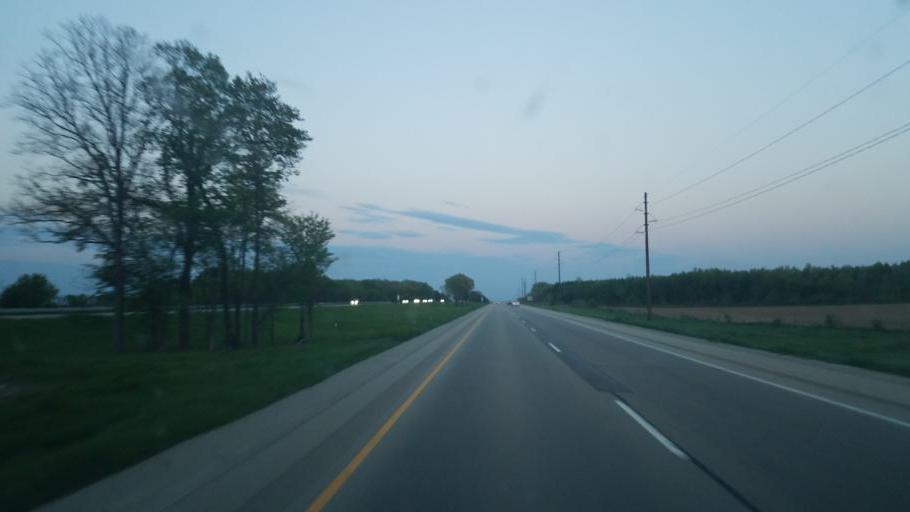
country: US
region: Wisconsin
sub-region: Jefferson County
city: Lake Mills
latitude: 43.1063
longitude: -88.9475
